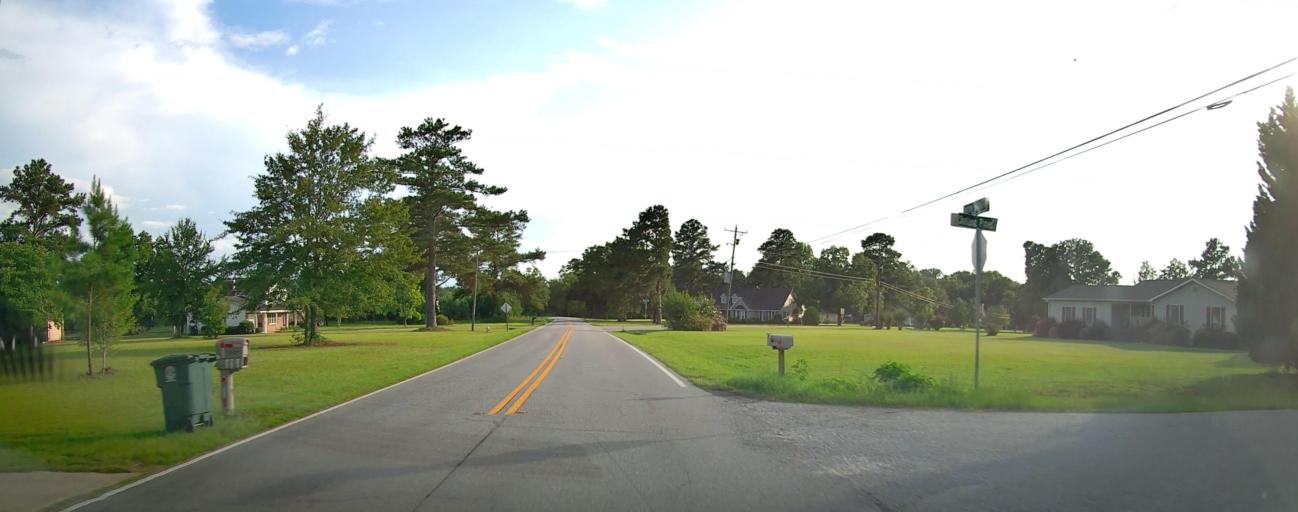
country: US
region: Georgia
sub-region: Peach County
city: Byron
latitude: 32.7339
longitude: -83.7390
